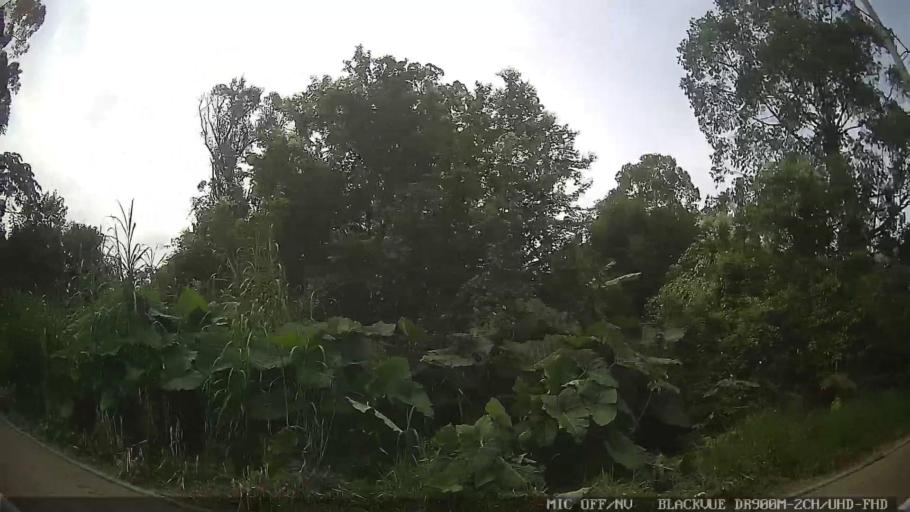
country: BR
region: Sao Paulo
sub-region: Poa
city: Poa
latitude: -23.5186
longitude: -46.3527
